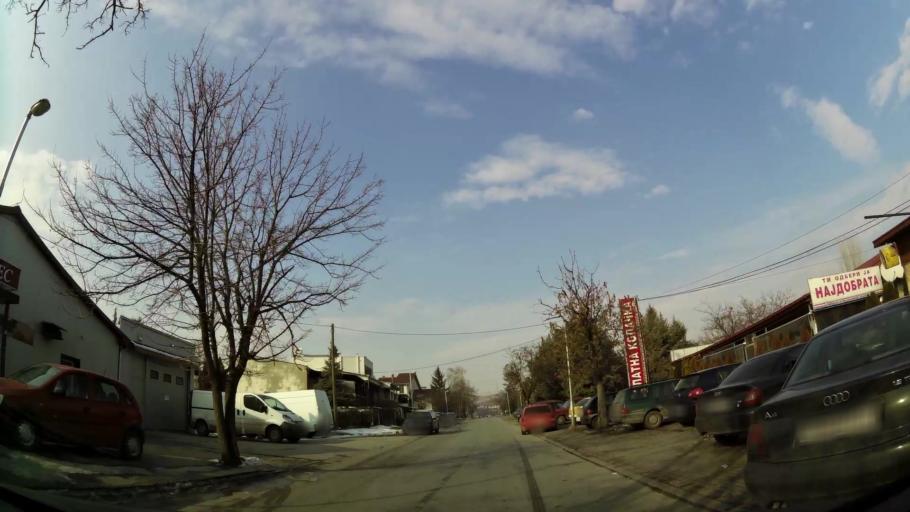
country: MK
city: Creshevo
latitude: 42.0073
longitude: 21.5027
